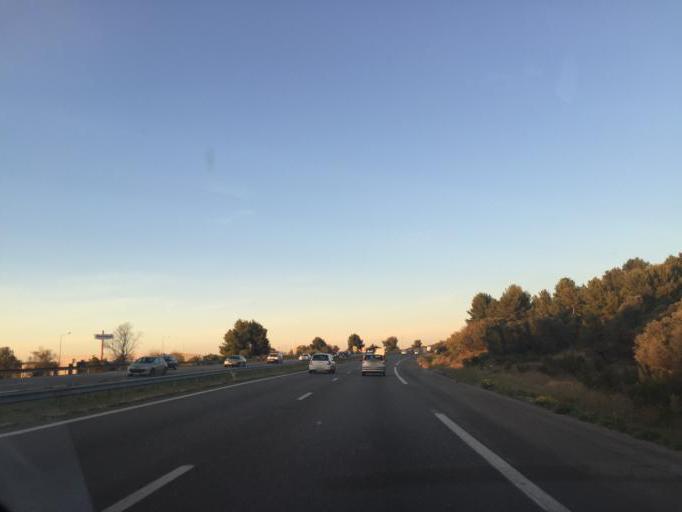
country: FR
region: Provence-Alpes-Cote d'Azur
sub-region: Departement des Bouches-du-Rhone
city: Rognac
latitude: 43.4701
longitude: 5.2341
